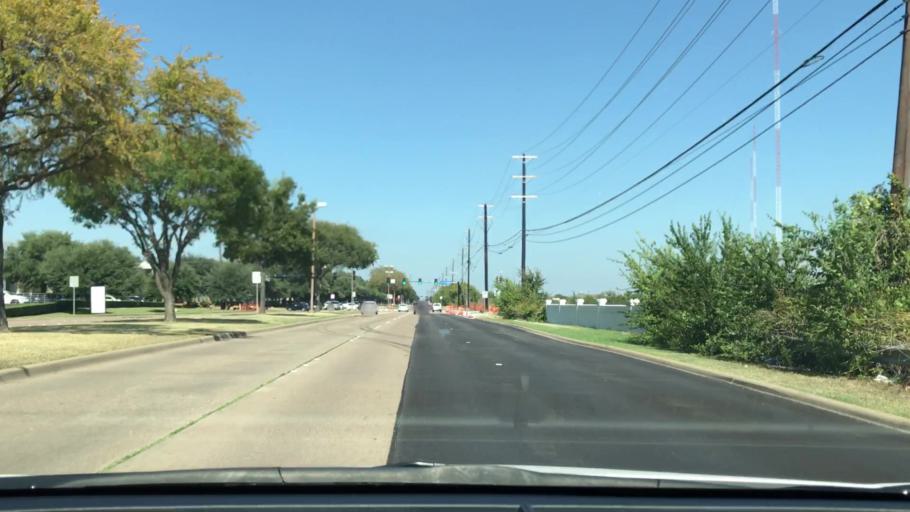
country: US
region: Texas
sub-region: Dallas County
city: Coppell
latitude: 32.9386
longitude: -96.9935
